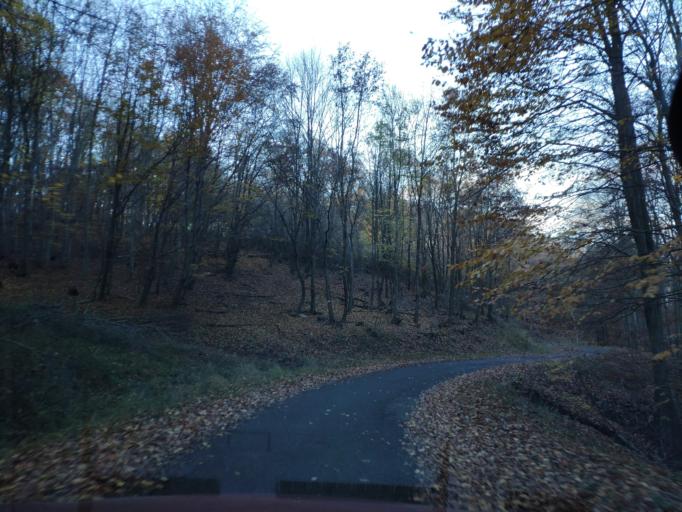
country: SK
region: Kosicky
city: Secovce
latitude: 48.5908
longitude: 21.5082
